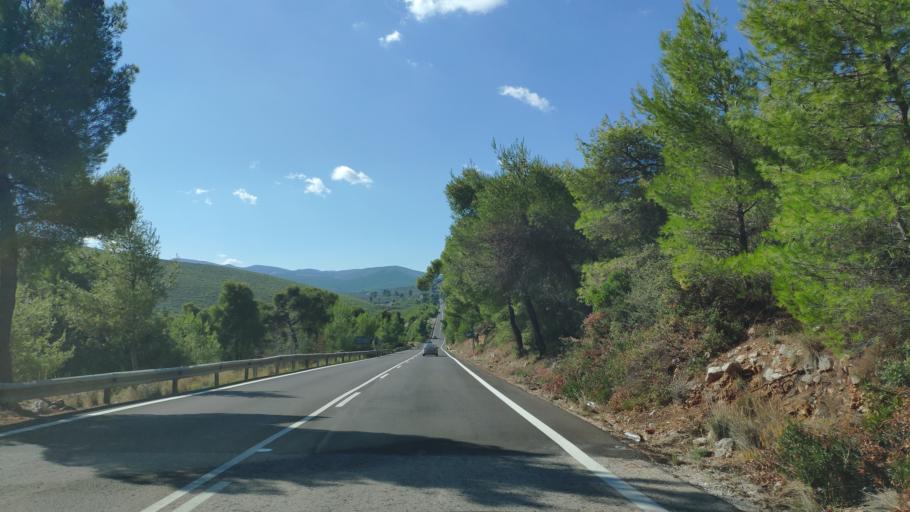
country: GR
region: Peloponnese
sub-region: Nomos Korinthias
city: Sofikon
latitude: 37.8214
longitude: 23.1022
